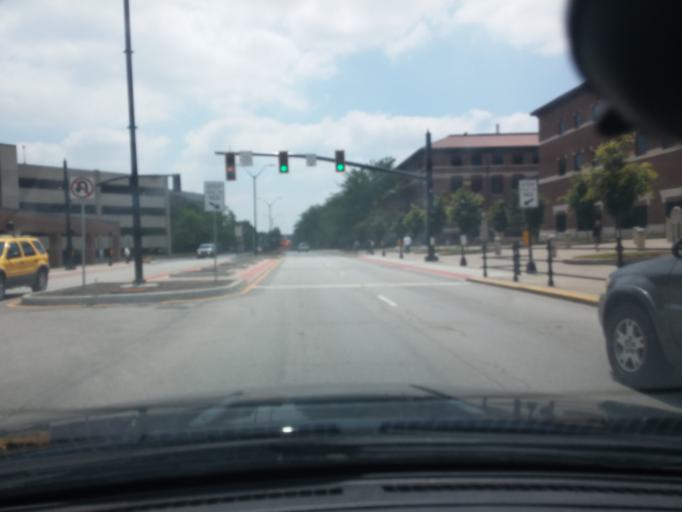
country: US
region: Indiana
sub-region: Tippecanoe County
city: West Lafayette
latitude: 40.4298
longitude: -86.9125
